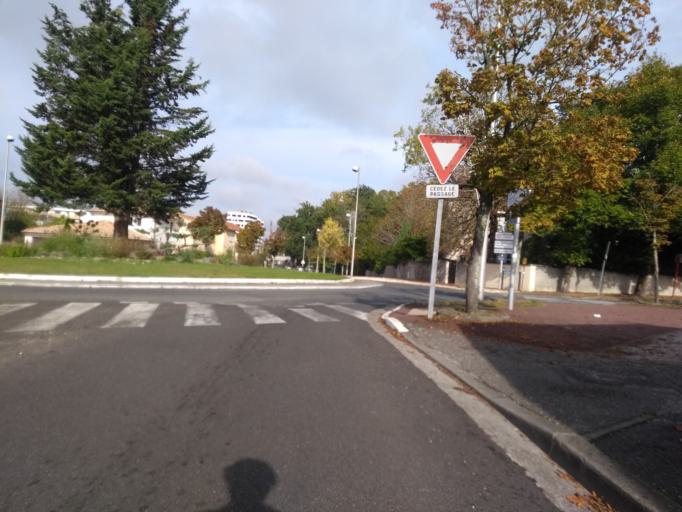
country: FR
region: Aquitaine
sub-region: Departement de la Gironde
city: Pessac
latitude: 44.7961
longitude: -0.6425
